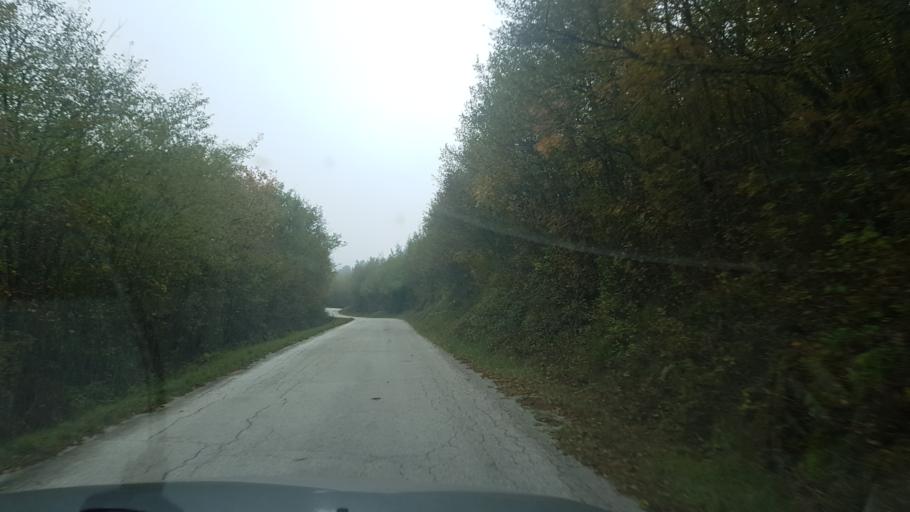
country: HR
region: Istarska
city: Buzet
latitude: 45.4580
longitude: 14.0344
